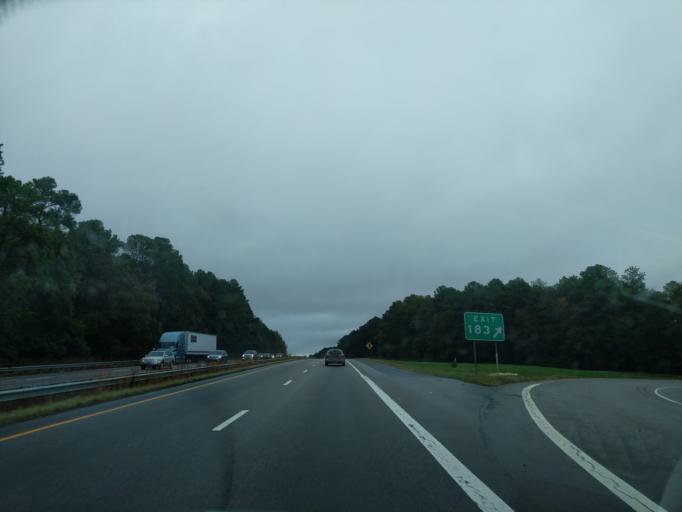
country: US
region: North Carolina
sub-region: Durham County
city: Gorman
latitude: 36.0584
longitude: -78.7944
